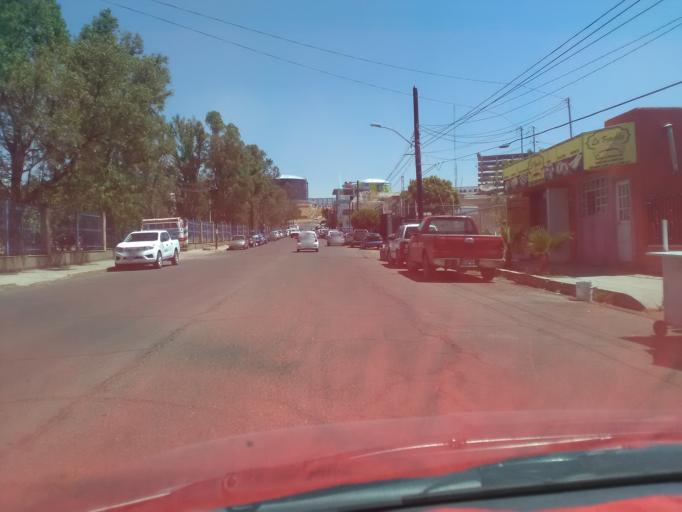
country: MX
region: Durango
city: Victoria de Durango
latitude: 24.0139
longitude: -104.6822
